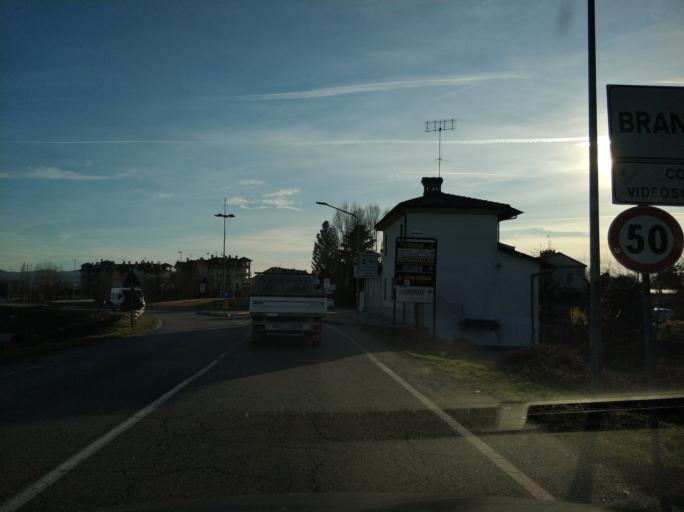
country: IT
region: Piedmont
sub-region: Provincia di Torino
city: Brandizzo
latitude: 45.1813
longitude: 7.8512
